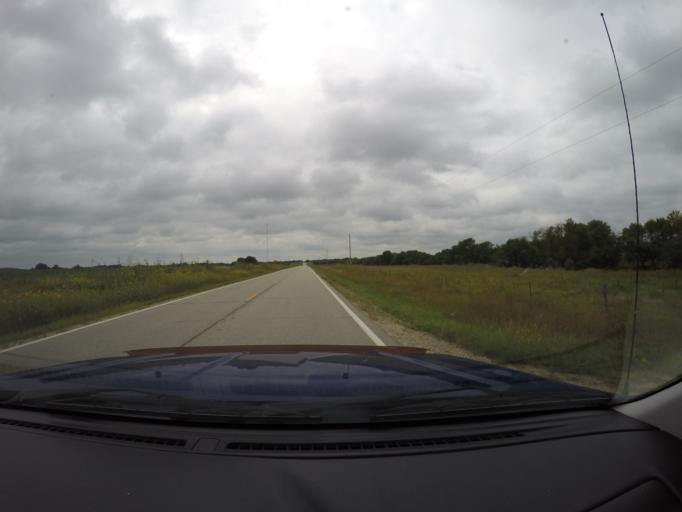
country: US
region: Kansas
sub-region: Morris County
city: Council Grove
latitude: 38.8409
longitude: -96.5481
